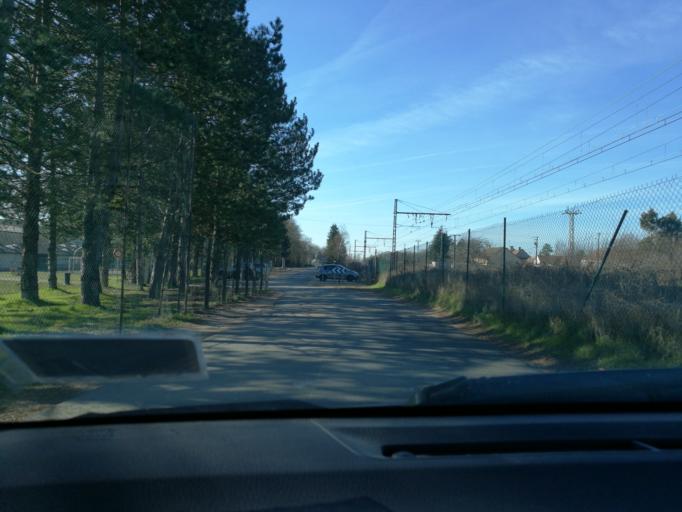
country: FR
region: Centre
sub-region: Departement du Loiret
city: Saint-Ay
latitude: 47.8646
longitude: 1.7530
